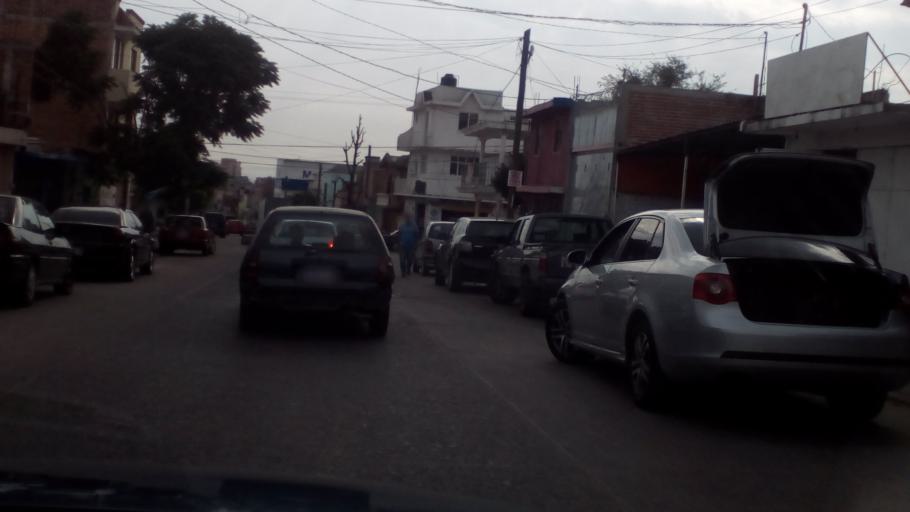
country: MX
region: Guanajuato
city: Leon
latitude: 21.1313
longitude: -101.6978
